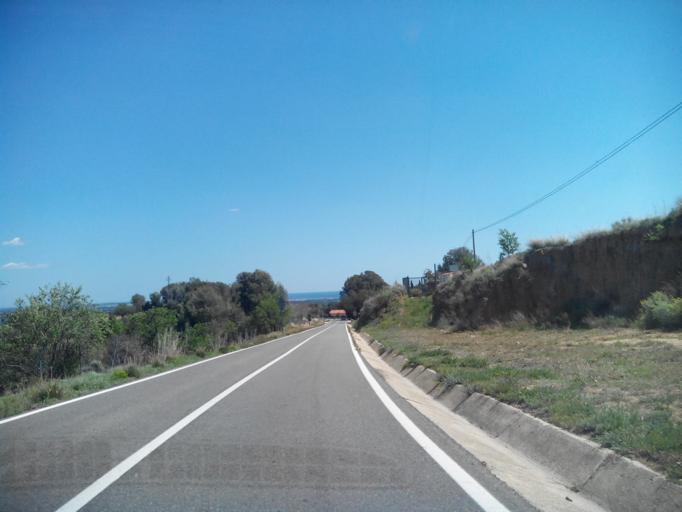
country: ES
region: Catalonia
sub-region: Provincia de Tarragona
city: Vilanova d'Escornalbou
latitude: 41.1109
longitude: 0.9469
